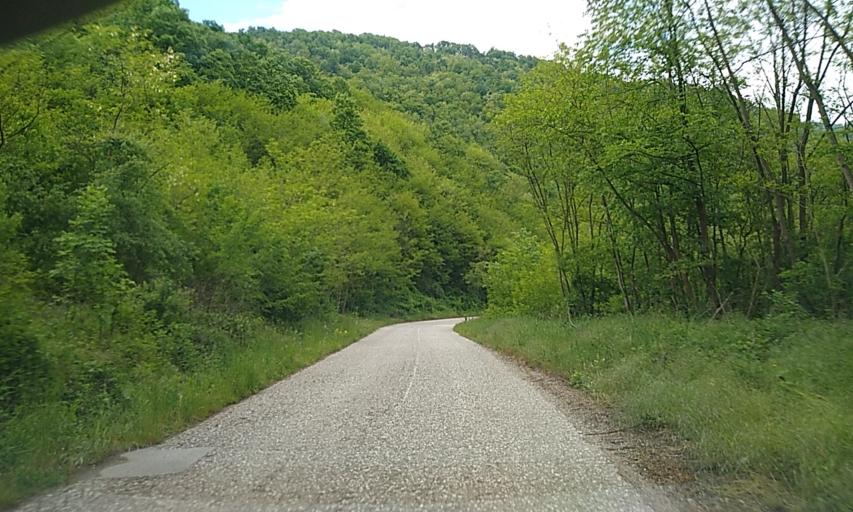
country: RS
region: Central Serbia
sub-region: Pcinjski Okrug
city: Vladicin Han
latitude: 42.7524
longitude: 22.0609
